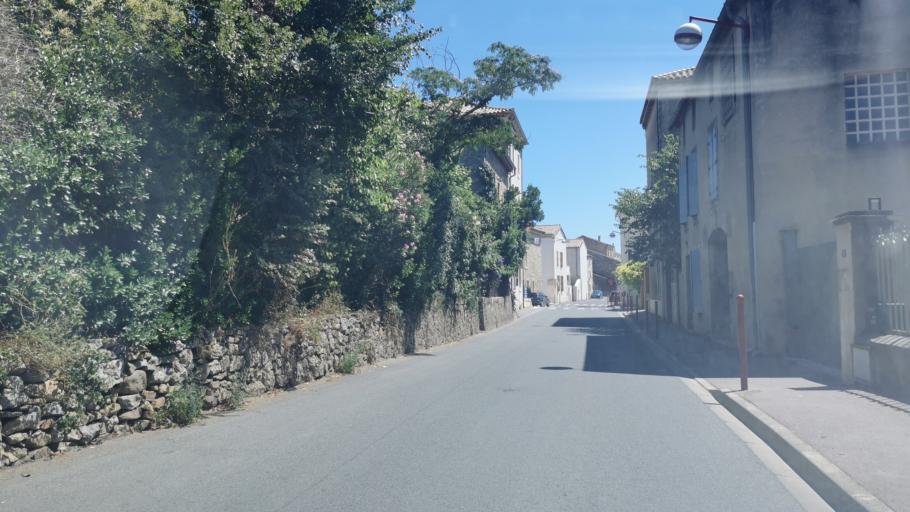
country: FR
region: Languedoc-Roussillon
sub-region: Departement de l'Aude
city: Vinassan
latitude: 43.2043
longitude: 3.0746
